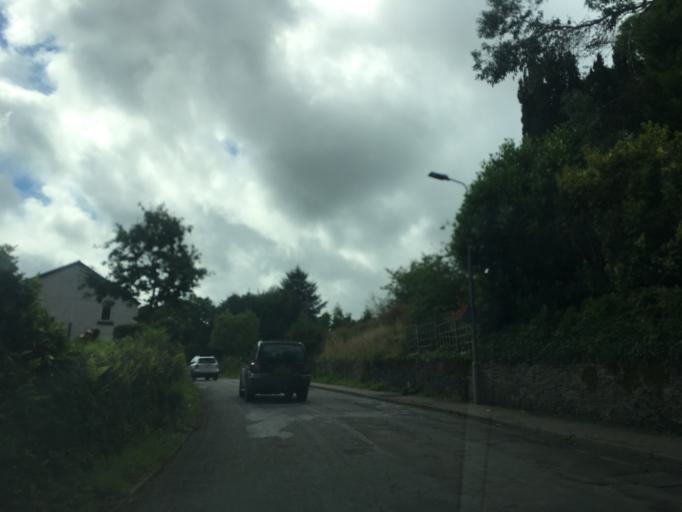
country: GB
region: Scotland
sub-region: Argyll and Bute
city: Tarbert
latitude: 55.8943
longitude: -5.2447
